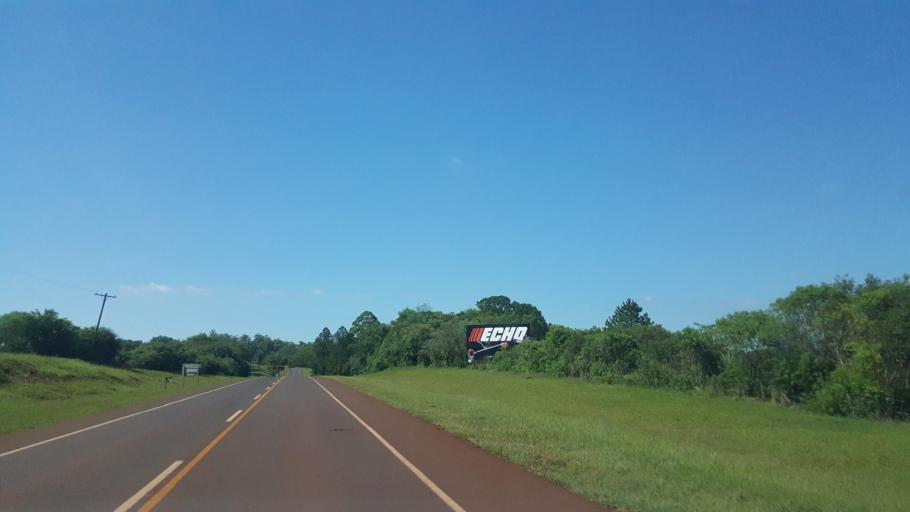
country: AR
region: Misiones
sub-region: Departamento de Apostoles
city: Apostoles
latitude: -27.8683
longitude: -55.7655
